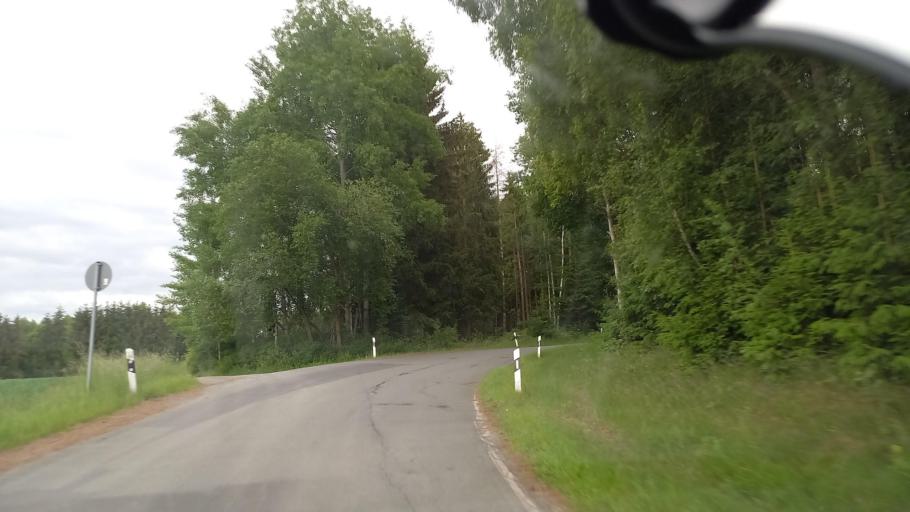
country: DE
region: Saxony
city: Waldkirchen
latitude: 50.6244
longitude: 12.4010
